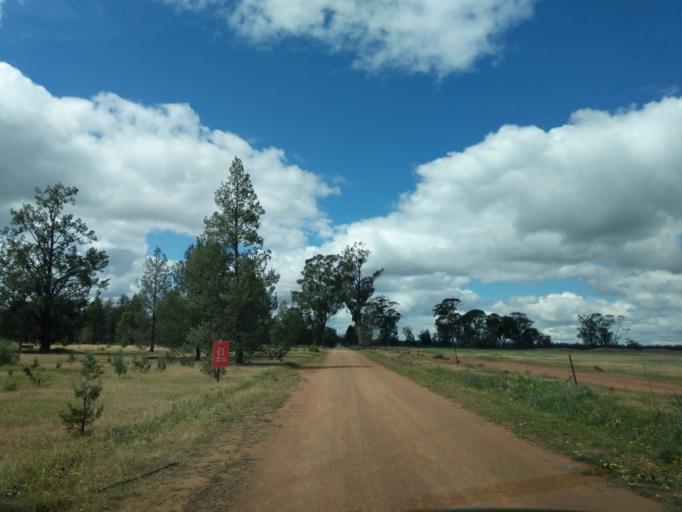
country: AU
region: New South Wales
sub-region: Coolamon
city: Coolamon
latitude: -34.8543
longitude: 146.9025
